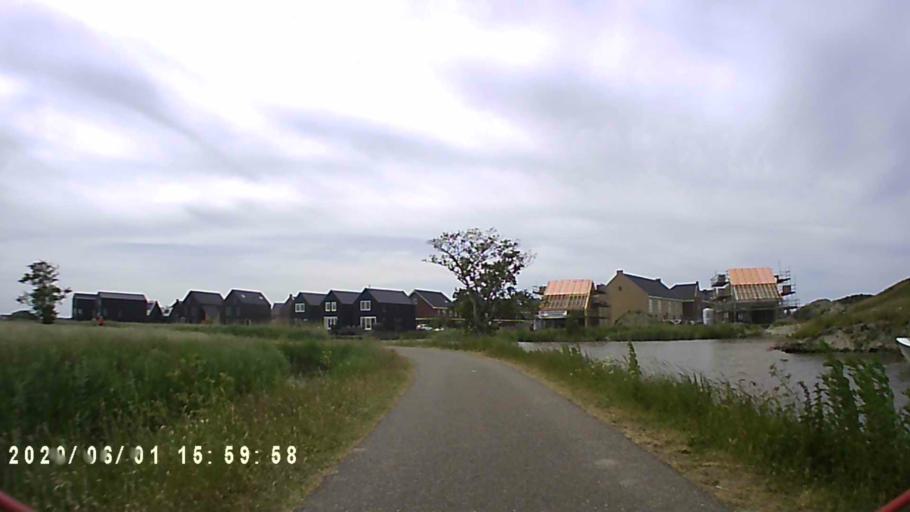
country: NL
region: Friesland
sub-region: Gemeente Leeuwarden
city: Goutum
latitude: 53.1719
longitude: 5.8240
